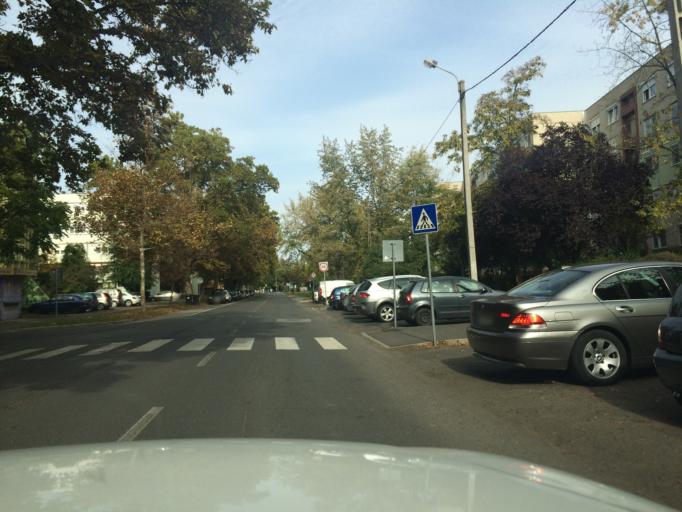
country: HU
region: Szabolcs-Szatmar-Bereg
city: Nyiregyhaza
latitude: 47.9629
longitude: 21.7115
